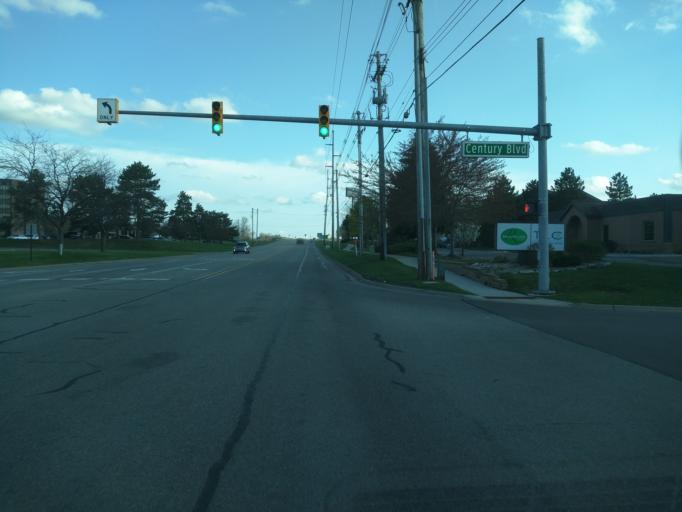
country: US
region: Michigan
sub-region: Eaton County
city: Waverly
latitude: 42.7246
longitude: -84.6424
